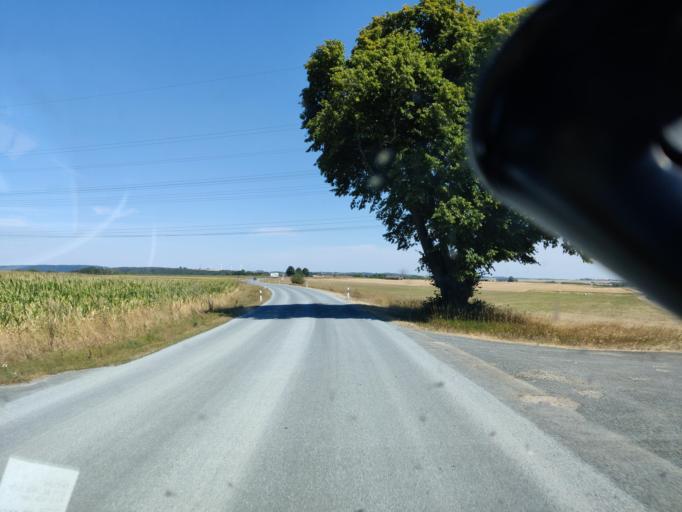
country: DE
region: Bavaria
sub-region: Regierungsbezirk Mittelfranken
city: Burgsalach
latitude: 49.0390
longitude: 11.1095
